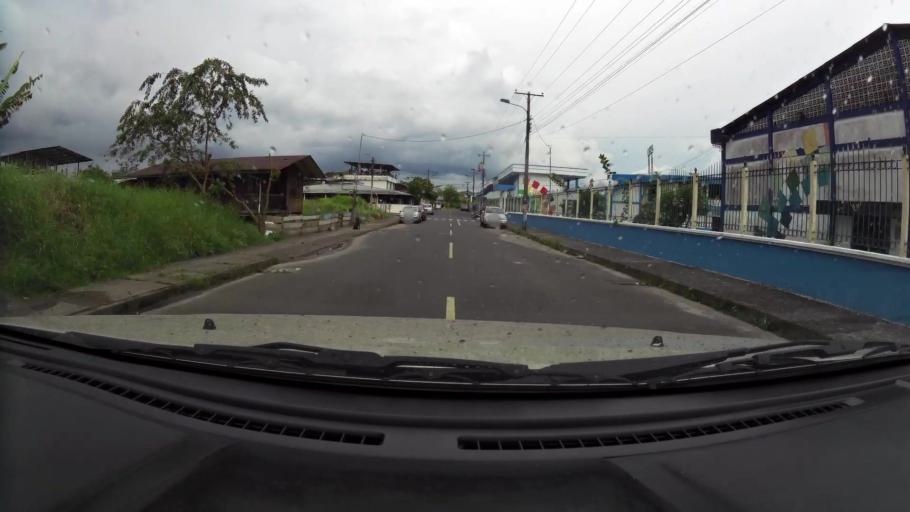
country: EC
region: Pastaza
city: Puyo
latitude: -1.4947
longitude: -78.0095
